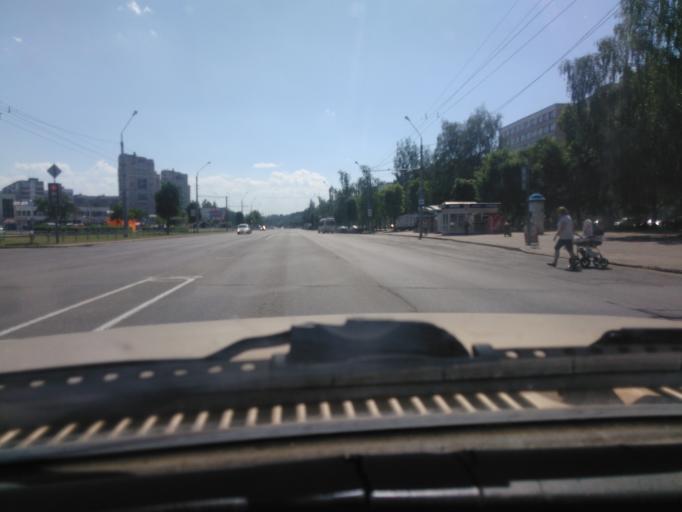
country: BY
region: Mogilev
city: Palykavichy Pyershyya
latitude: 53.9520
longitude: 30.3608
